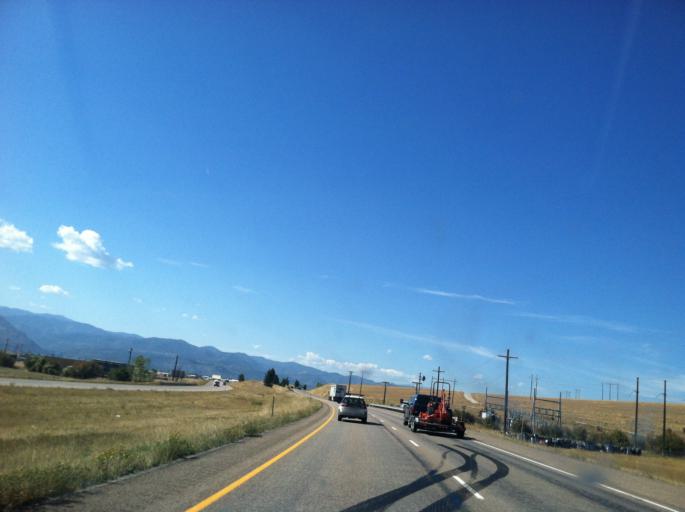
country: US
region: Montana
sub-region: Missoula County
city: Orchard Homes
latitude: 46.9377
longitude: -114.0977
